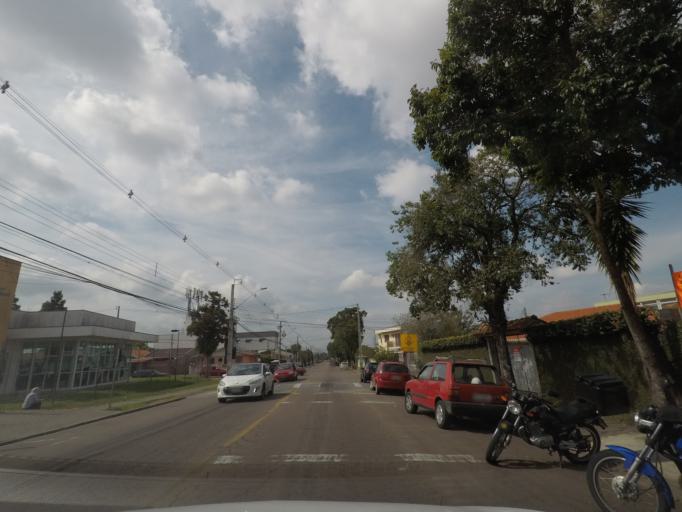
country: BR
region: Parana
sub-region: Pinhais
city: Pinhais
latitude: -25.4698
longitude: -49.2065
